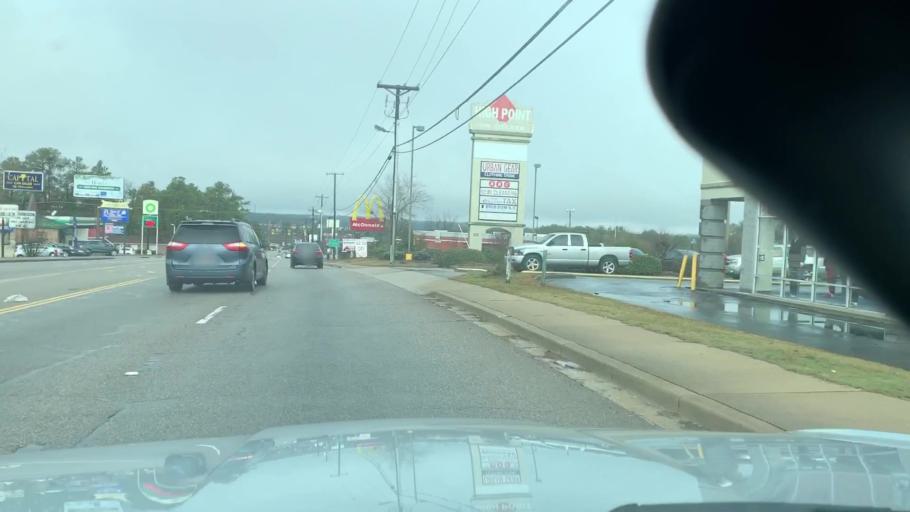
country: US
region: South Carolina
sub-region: Richland County
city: Woodfield
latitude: 34.0524
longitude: -80.9456
